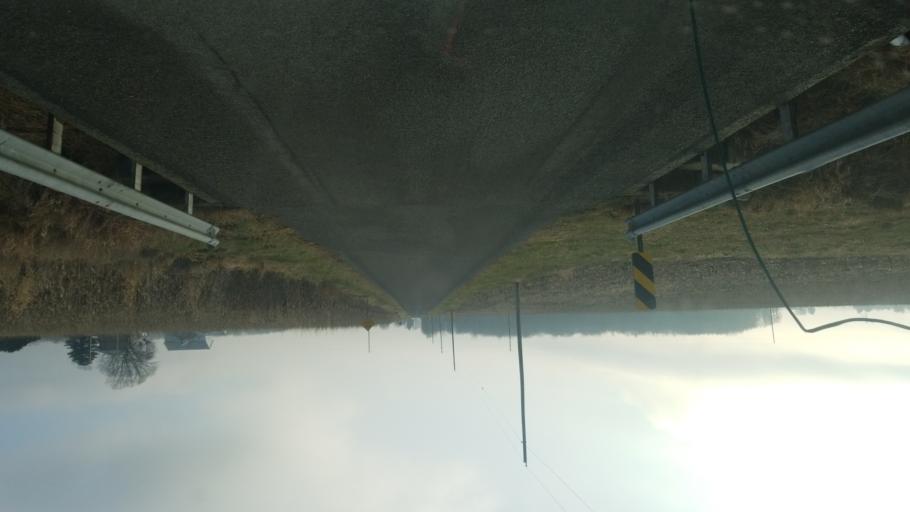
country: US
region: Ohio
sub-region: Hardin County
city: Kenton
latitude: 40.6885
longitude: -83.5927
